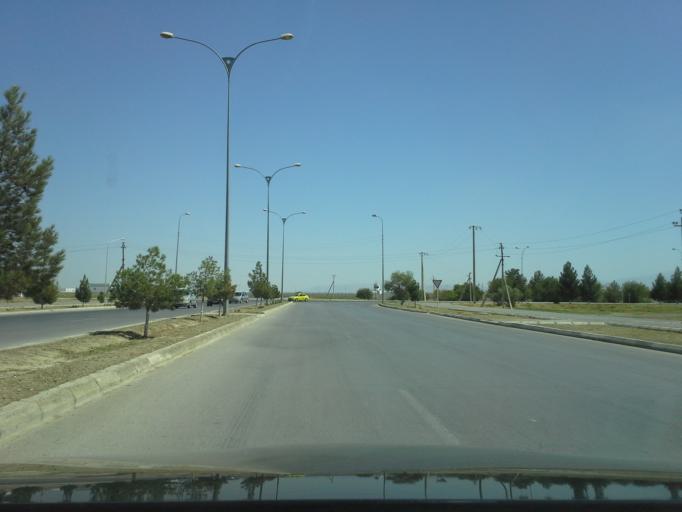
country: TM
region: Ahal
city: Ashgabat
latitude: 37.9978
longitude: 58.3245
